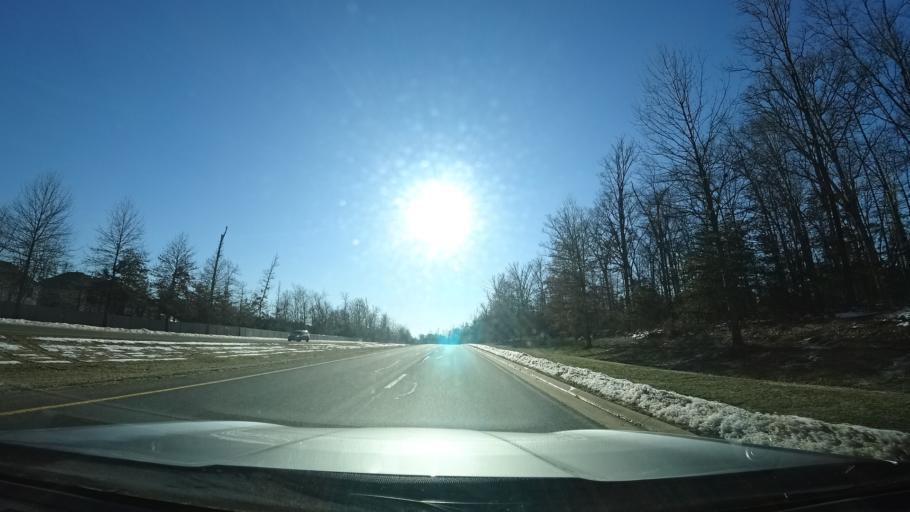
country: US
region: Virginia
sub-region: Loudoun County
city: Belmont
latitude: 39.0637
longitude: -77.5003
